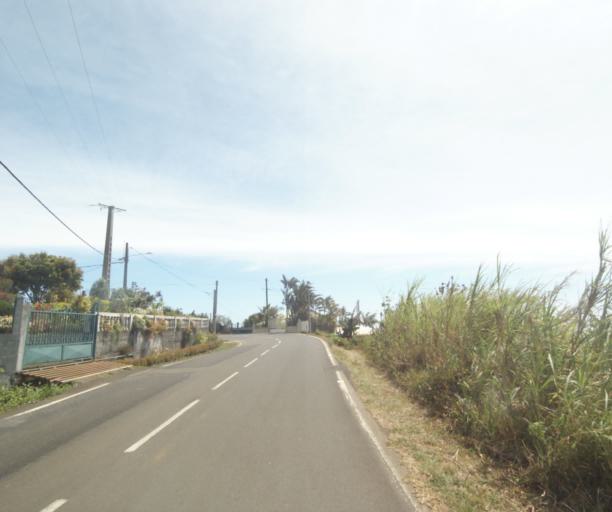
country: RE
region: Reunion
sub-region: Reunion
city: Trois-Bassins
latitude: -21.0625
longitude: 55.3079
